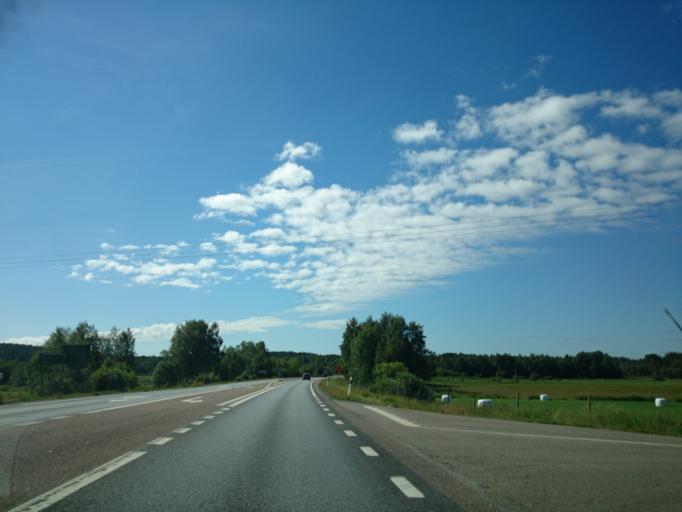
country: SE
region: Gaevleborg
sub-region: Soderhamns Kommun
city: Soderhamn
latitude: 61.2810
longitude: 17.0270
